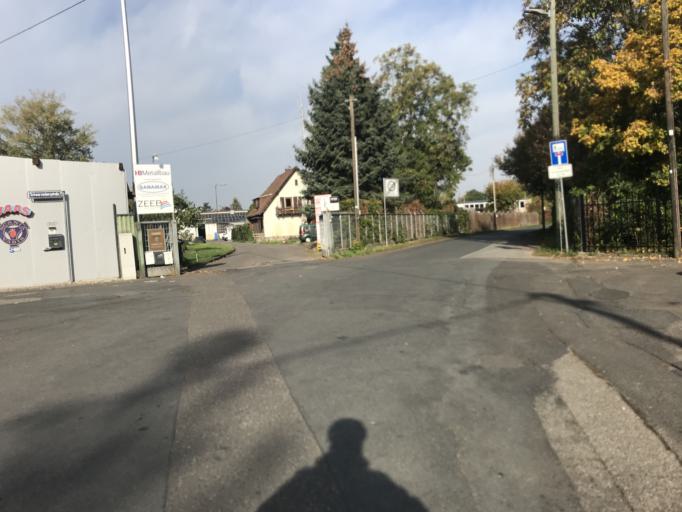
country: DE
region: Rheinland-Pfalz
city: Mainz
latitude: 50.0145
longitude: 8.2807
